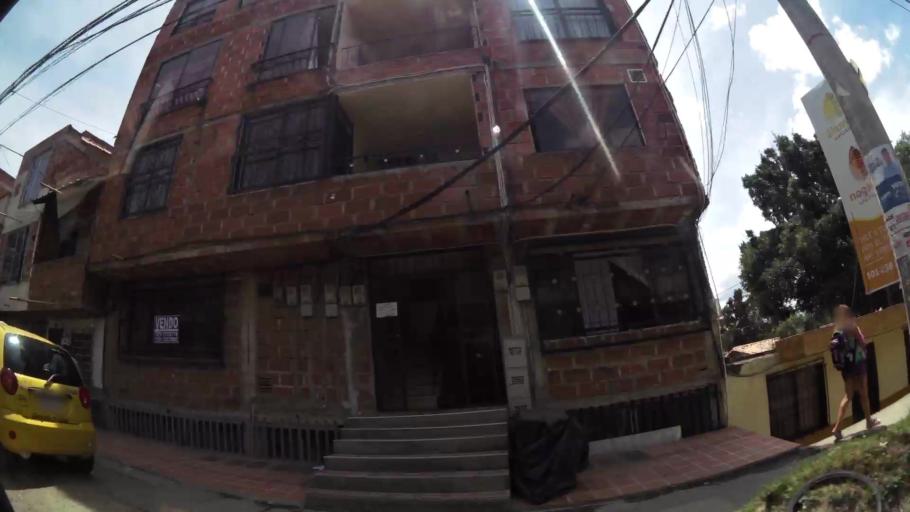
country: CO
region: Antioquia
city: Bello
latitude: 6.3459
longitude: -75.5684
